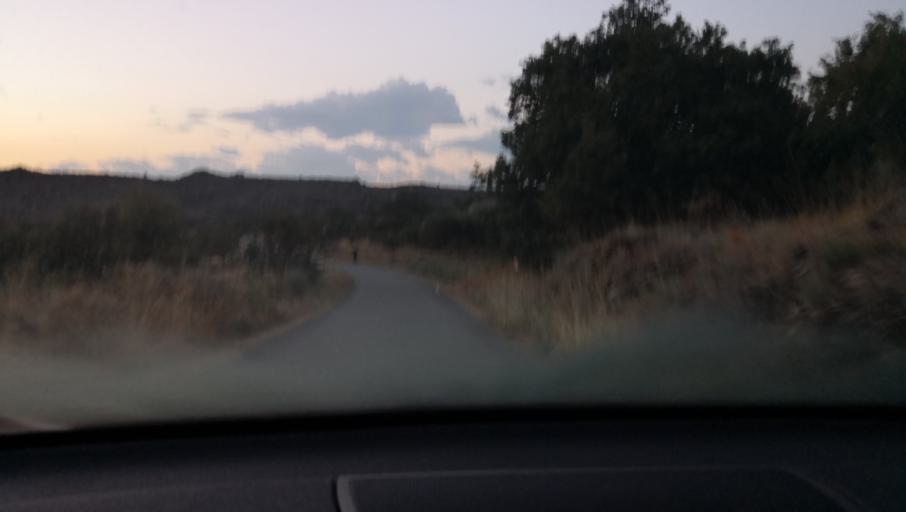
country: PT
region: Vila Real
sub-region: Sabrosa
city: Sabrosa
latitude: 41.2957
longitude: -7.6183
